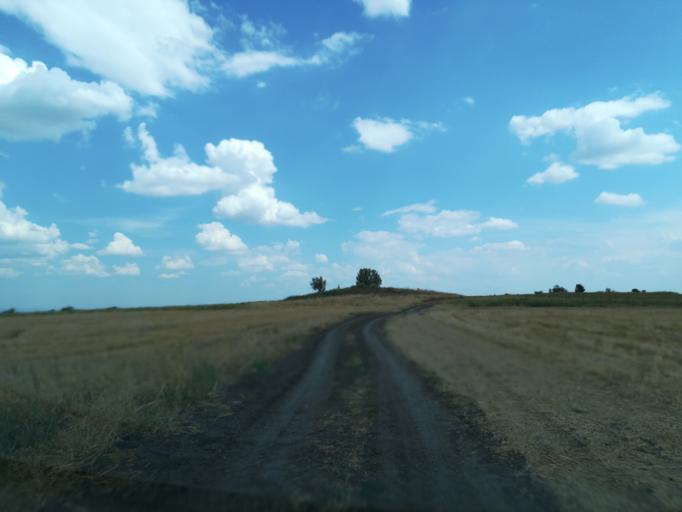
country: BG
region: Khaskovo
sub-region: Obshtina Mineralni Bani
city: Mineralni Bani
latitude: 42.0032
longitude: 25.2012
